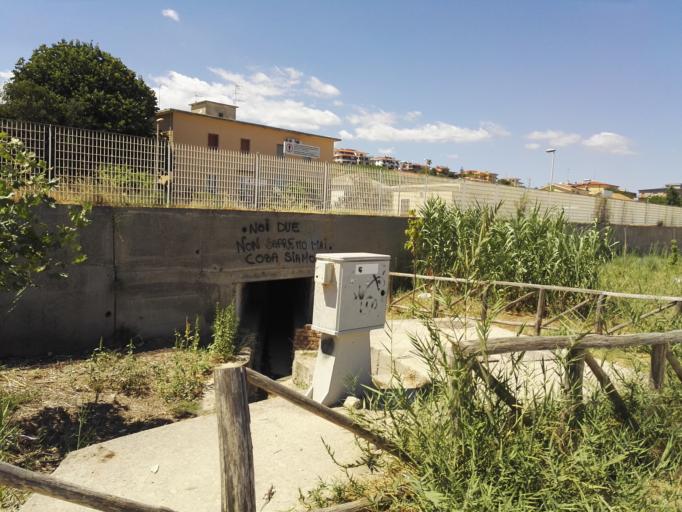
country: IT
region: Calabria
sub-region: Provincia di Catanzaro
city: Santa Caterina dello Ionio Marina
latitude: 38.5299
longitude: 16.5715
